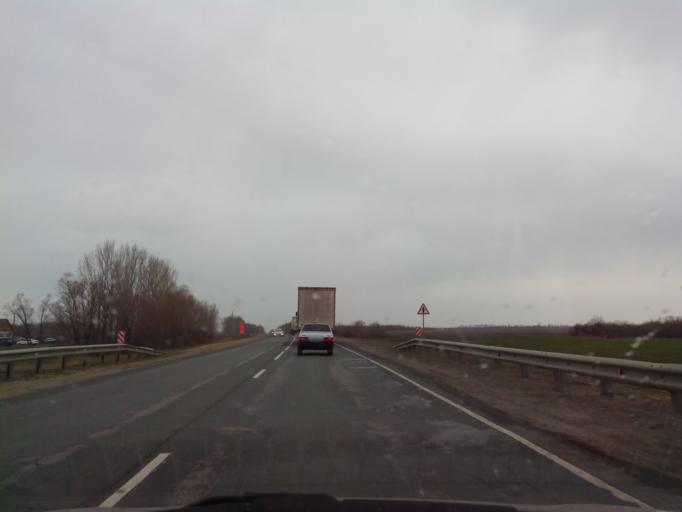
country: RU
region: Tambov
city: Pervomayskiy
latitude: 53.1133
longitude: 40.3917
